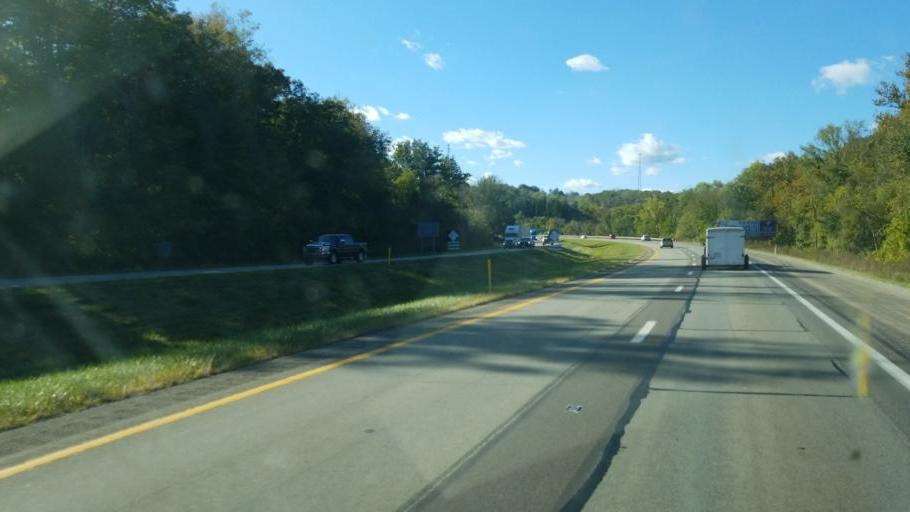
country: US
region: West Virginia
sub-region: Brooke County
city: Bethany
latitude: 40.1173
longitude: -80.4699
